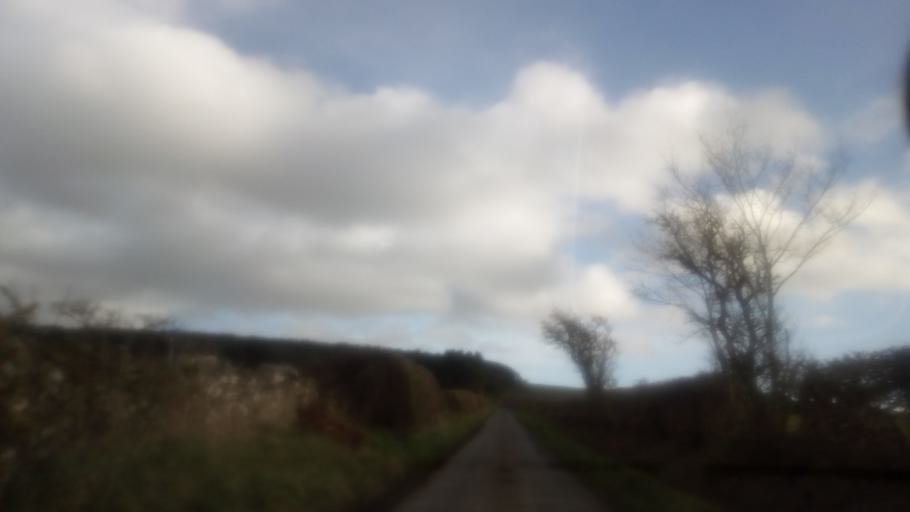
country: GB
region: Scotland
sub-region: The Scottish Borders
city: Jedburgh
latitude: 55.4837
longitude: -2.6081
